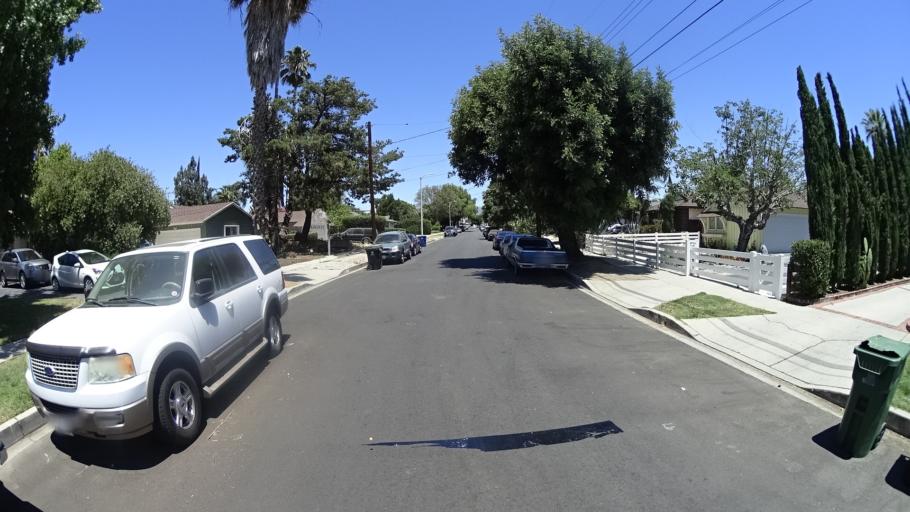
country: US
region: California
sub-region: Los Angeles County
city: Van Nuys
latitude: 34.2256
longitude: -118.4710
